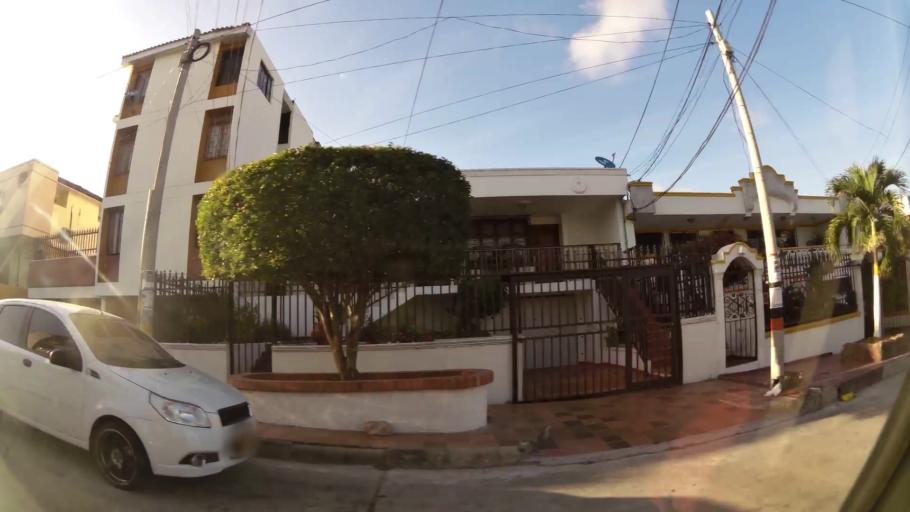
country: CO
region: Atlantico
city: Barranquilla
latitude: 10.9852
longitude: -74.8047
